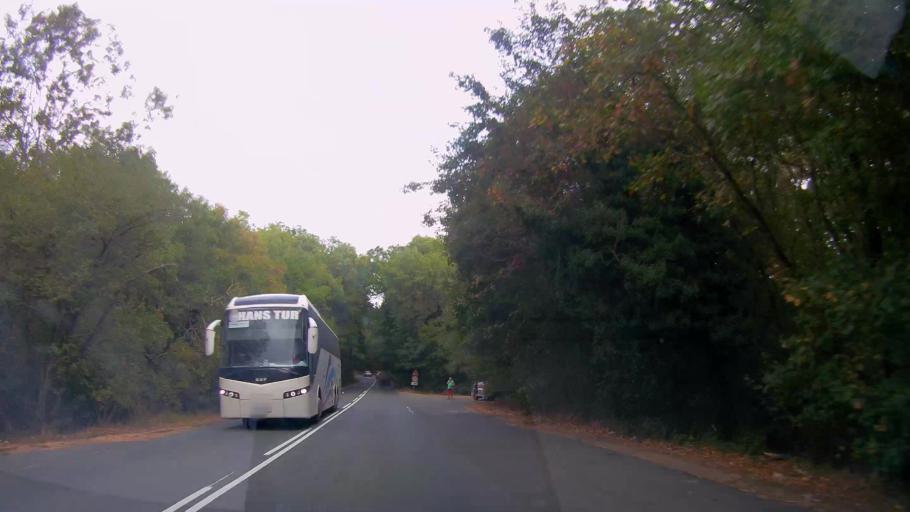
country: BG
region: Burgas
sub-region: Obshtina Primorsko
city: Primorsko
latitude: 42.3002
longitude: 27.7294
